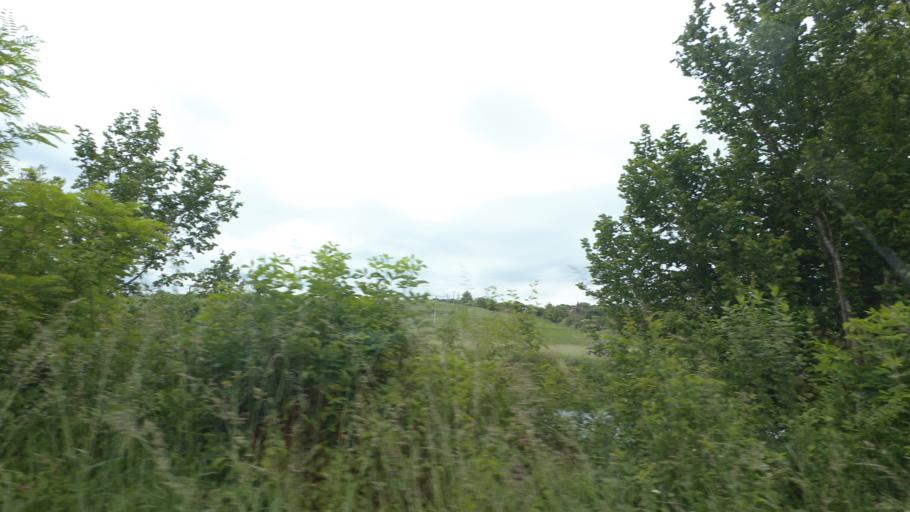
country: HR
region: Karlovacka
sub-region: Grad Karlovac
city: Karlovac
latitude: 45.4252
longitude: 15.5650
